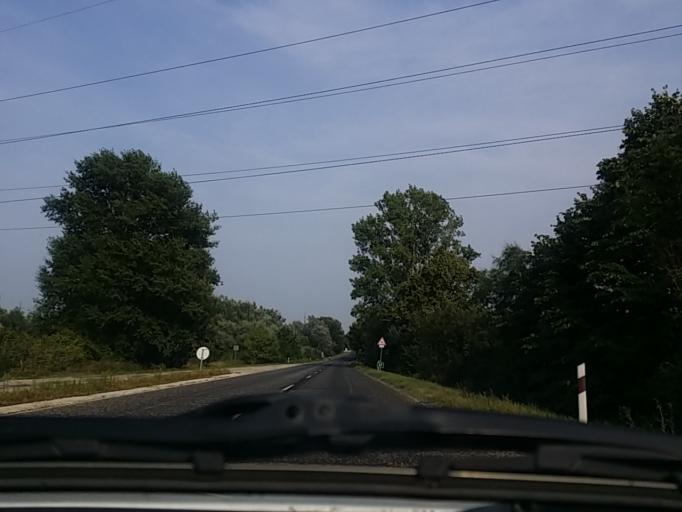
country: HU
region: Fejer
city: Bicske
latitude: 47.4950
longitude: 18.6840
